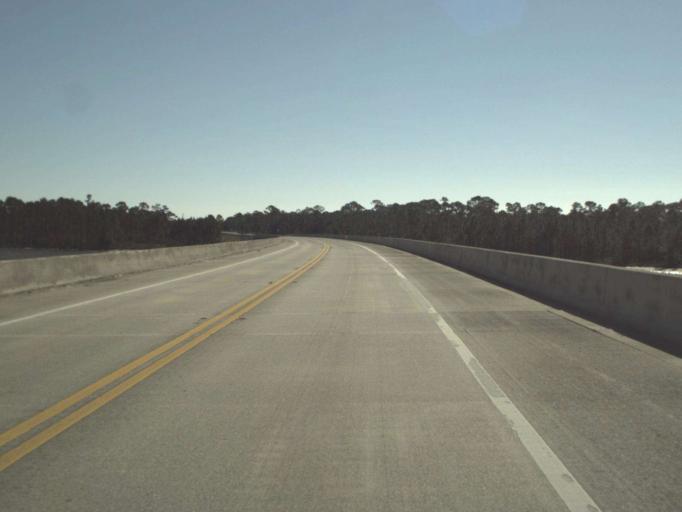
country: US
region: Florida
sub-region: Santa Rosa County
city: Oriole Beach
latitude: 30.4010
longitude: -87.0789
